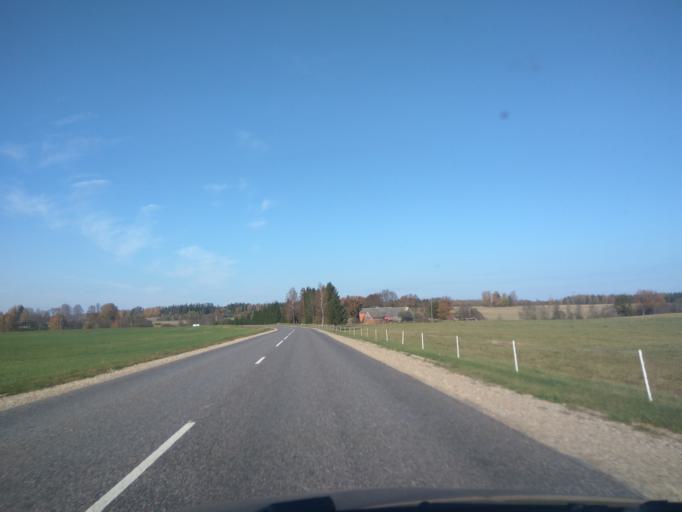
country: LV
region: Kuldigas Rajons
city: Kuldiga
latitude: 57.0152
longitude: 21.8767
